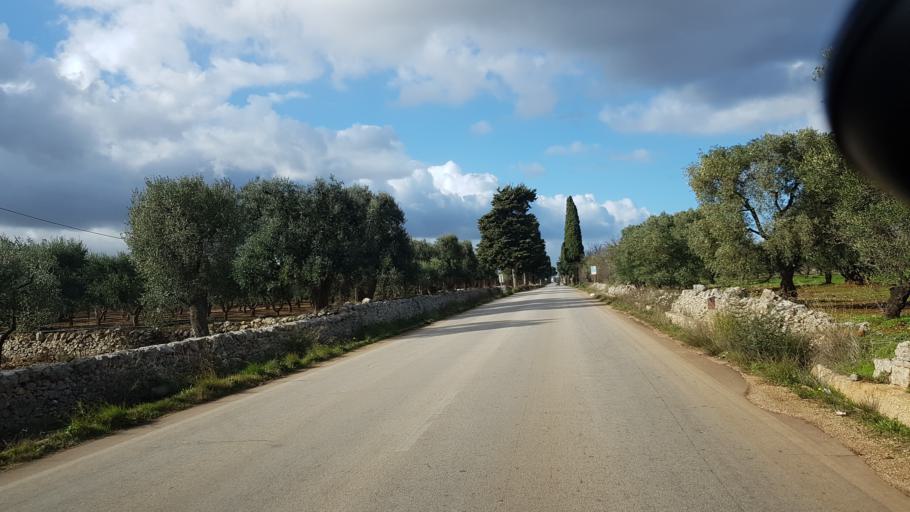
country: IT
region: Apulia
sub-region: Provincia di Brindisi
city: Montalbano
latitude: 40.7770
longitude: 17.4925
